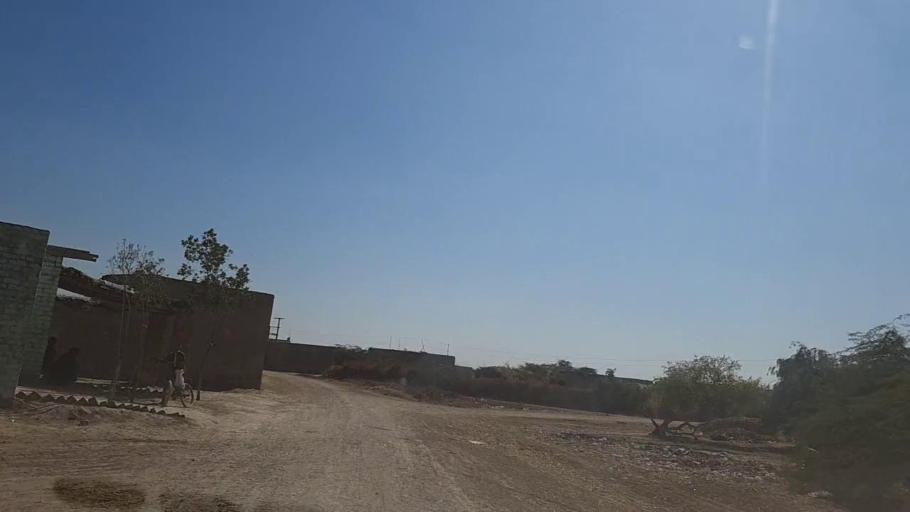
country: PK
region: Sindh
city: Digri
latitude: 25.1002
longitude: 69.1280
